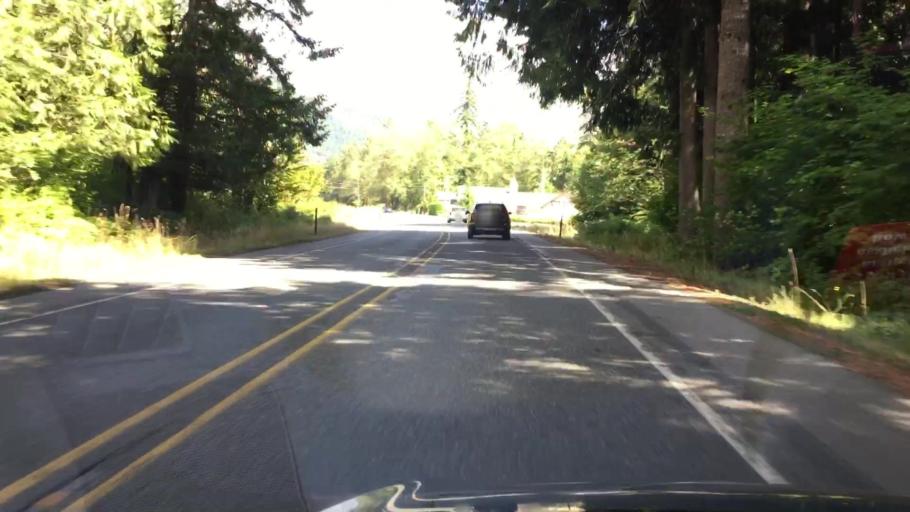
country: US
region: Washington
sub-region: Pierce County
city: Eatonville
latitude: 46.7565
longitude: -122.0578
